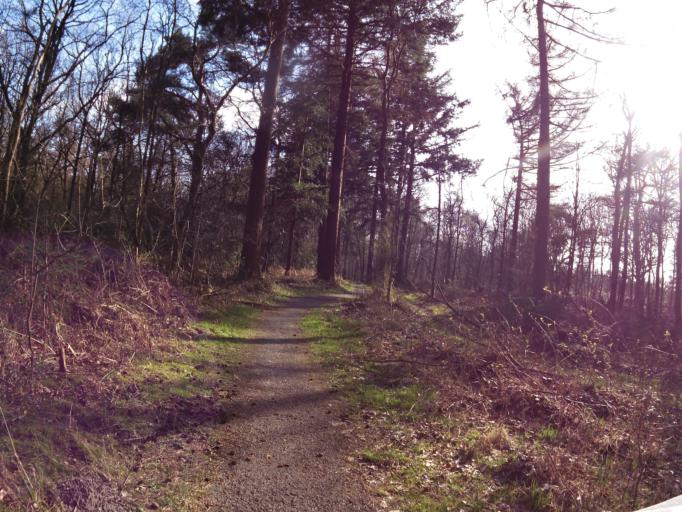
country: NL
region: Overijssel
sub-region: Gemeente Steenwijkerland
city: Tuk
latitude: 52.8216
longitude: 6.1138
